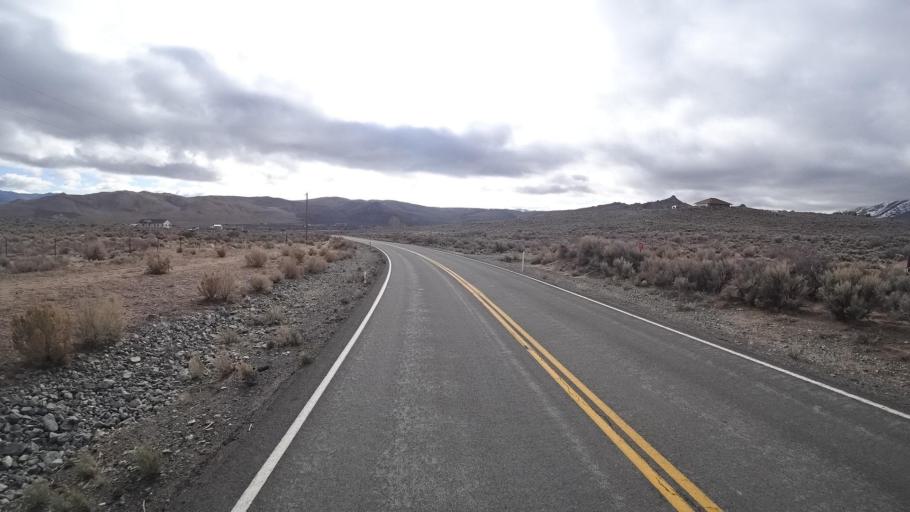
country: US
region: Nevada
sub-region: Washoe County
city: Cold Springs
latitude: 39.8682
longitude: -119.9501
